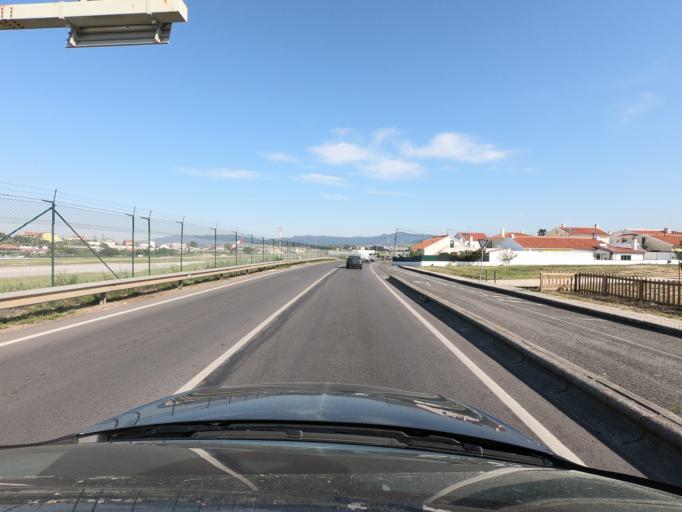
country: PT
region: Lisbon
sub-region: Cascais
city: Parede
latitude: 38.7264
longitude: -9.3542
